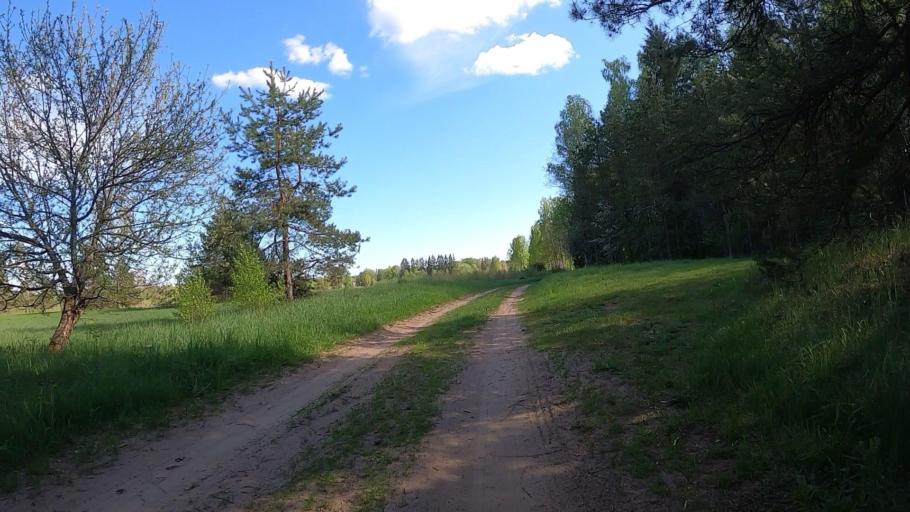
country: LV
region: Baldone
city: Baldone
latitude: 56.7705
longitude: 24.4297
